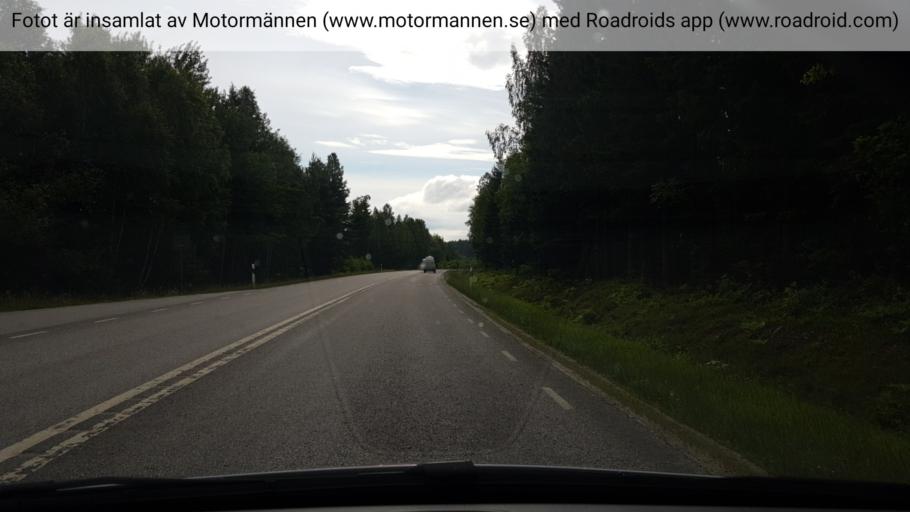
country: SE
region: Vaestra Goetaland
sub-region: Karlsborgs Kommun
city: Molltorp
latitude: 58.4908
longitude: 14.3790
